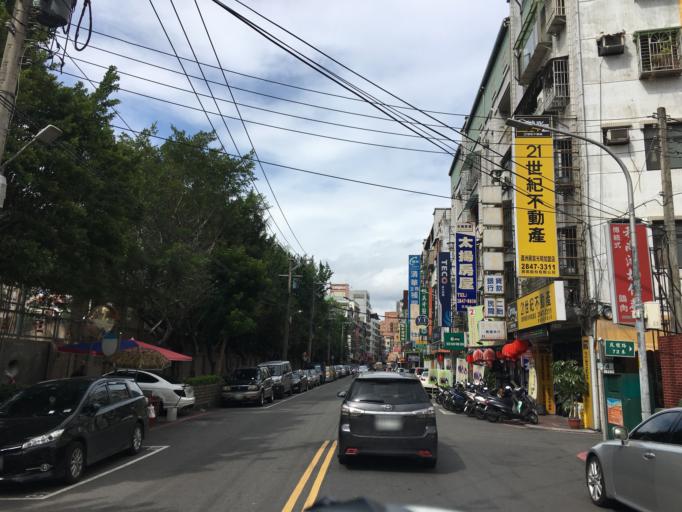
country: TW
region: Taipei
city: Taipei
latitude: 25.0875
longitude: 121.4751
